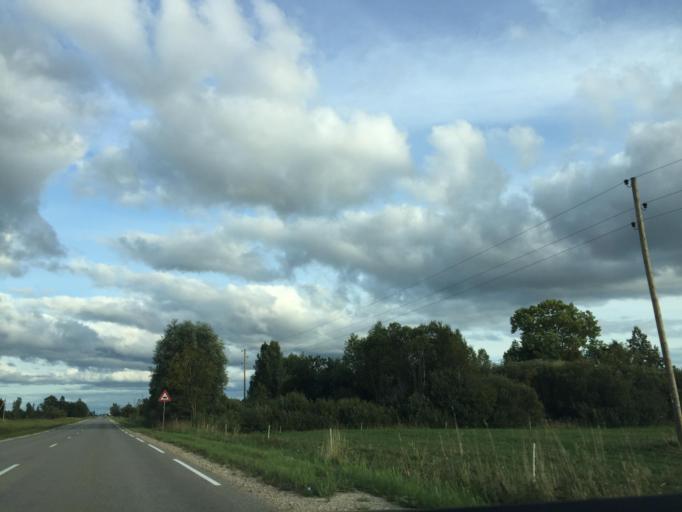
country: LV
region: Nereta
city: Nereta
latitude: 56.2567
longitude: 25.2027
